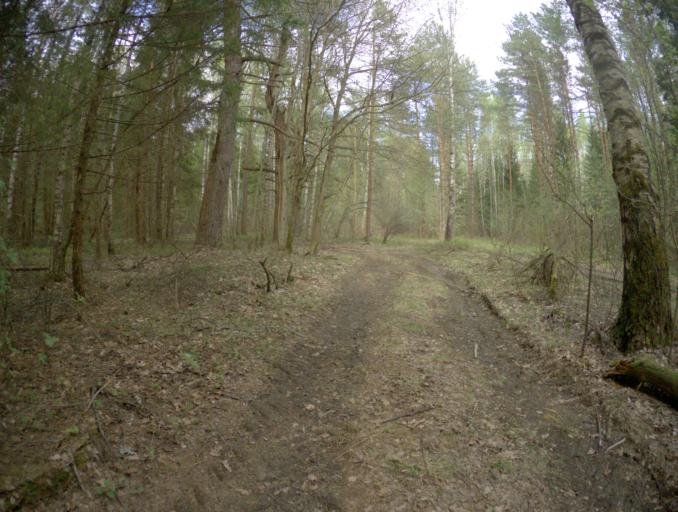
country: RU
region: Vladimir
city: Golovino
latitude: 55.9080
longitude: 40.4987
